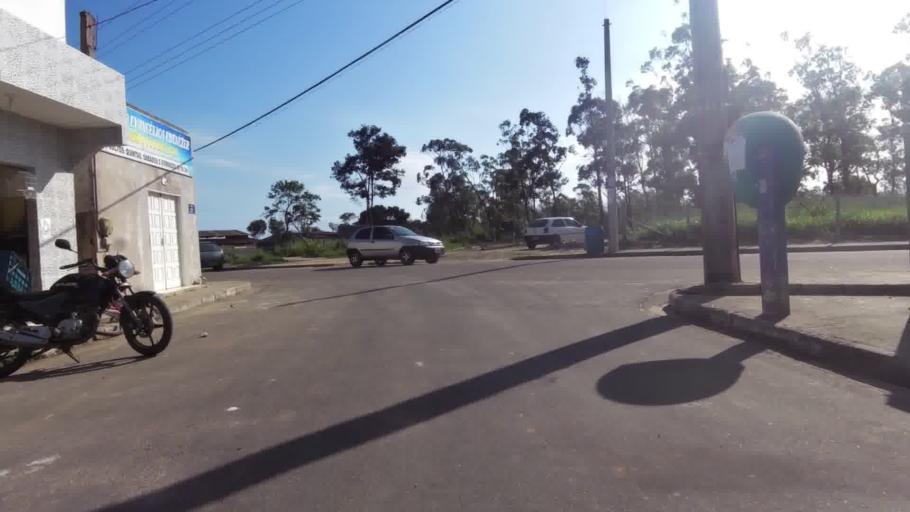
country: BR
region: Espirito Santo
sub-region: Piuma
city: Piuma
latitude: -20.8177
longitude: -40.6246
